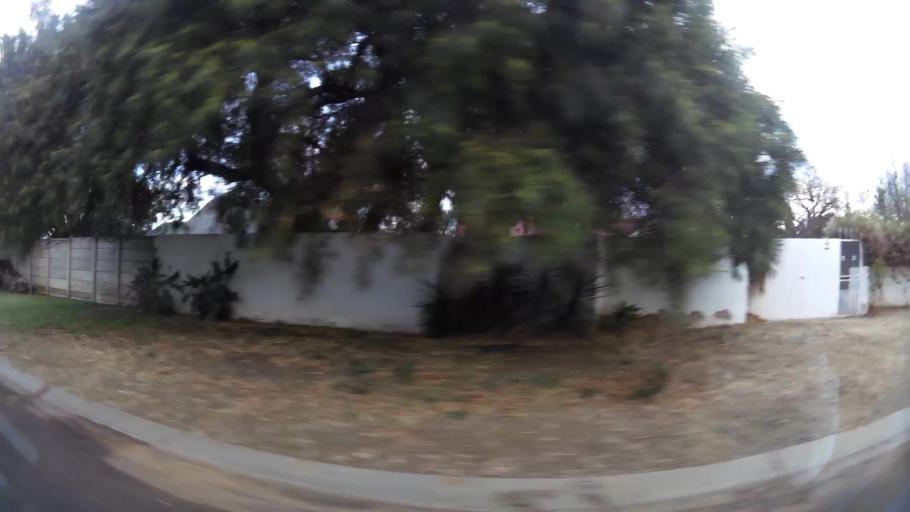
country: ZA
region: Orange Free State
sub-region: Lejweleputswa District Municipality
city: Welkom
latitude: -27.9783
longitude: 26.7229
